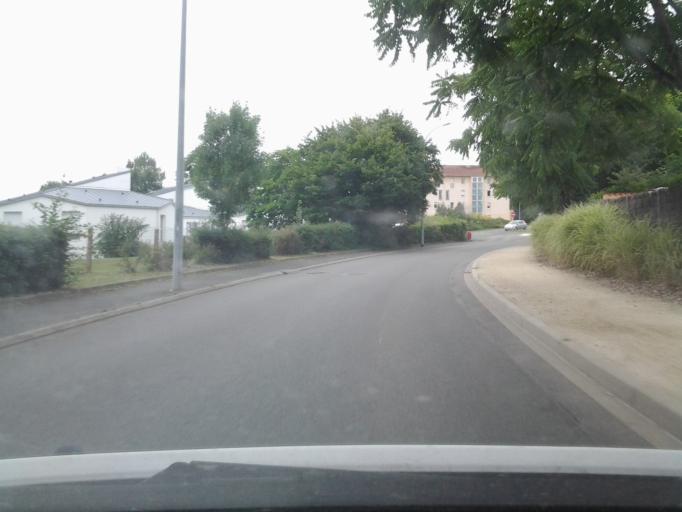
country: FR
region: Pays de la Loire
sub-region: Departement de la Vendee
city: La Roche-sur-Yon
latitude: 46.6550
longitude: -1.4241
